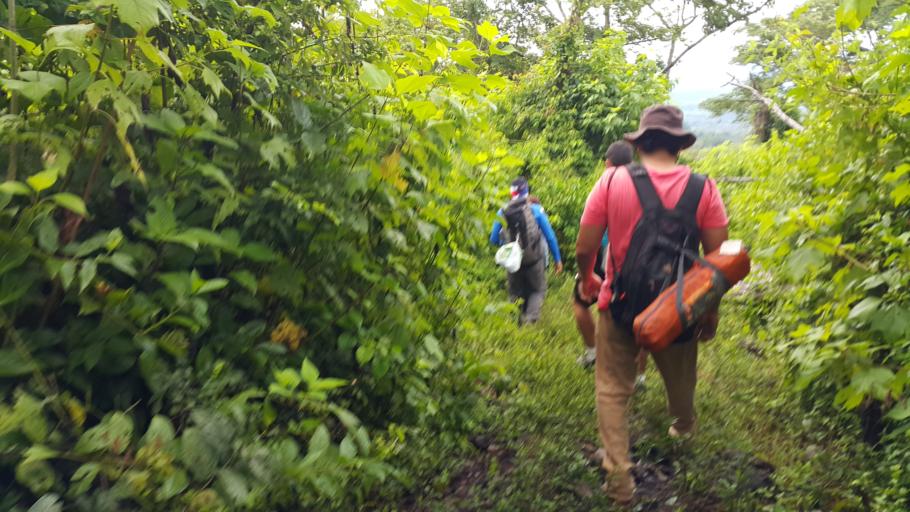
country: NI
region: Chinandega
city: Jiquilillo
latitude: 12.9741
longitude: -87.5523
